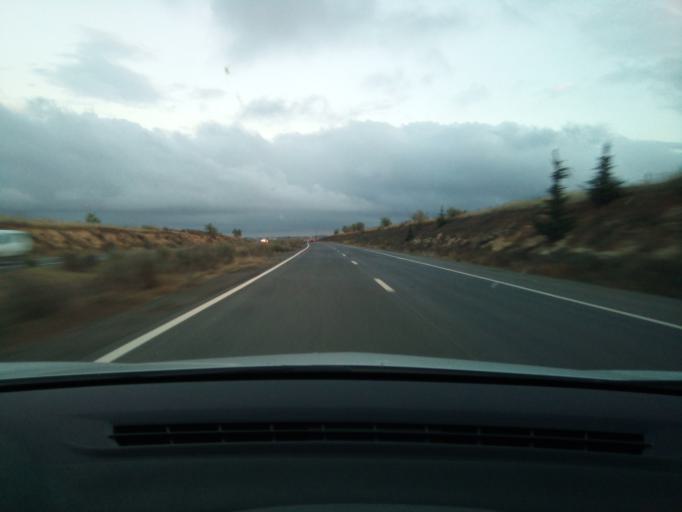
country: MA
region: Meknes-Tafilalet
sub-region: Meknes
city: Meknes
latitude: 33.8684
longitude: -5.6430
